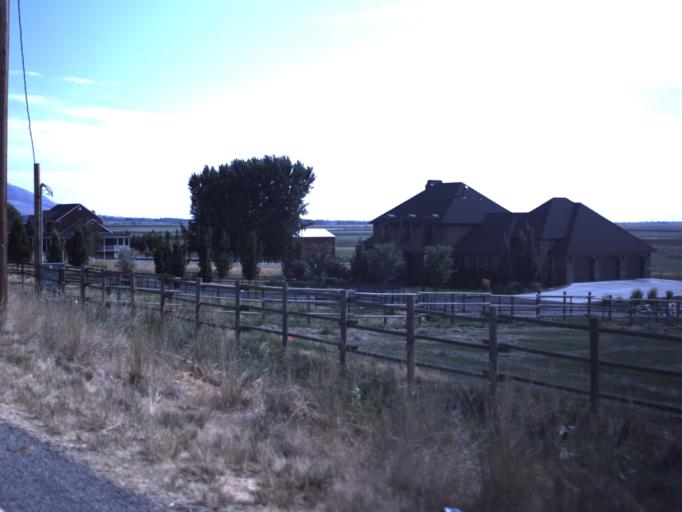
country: US
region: Utah
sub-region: Box Elder County
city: Brigham City
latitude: 41.5730
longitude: -112.0305
